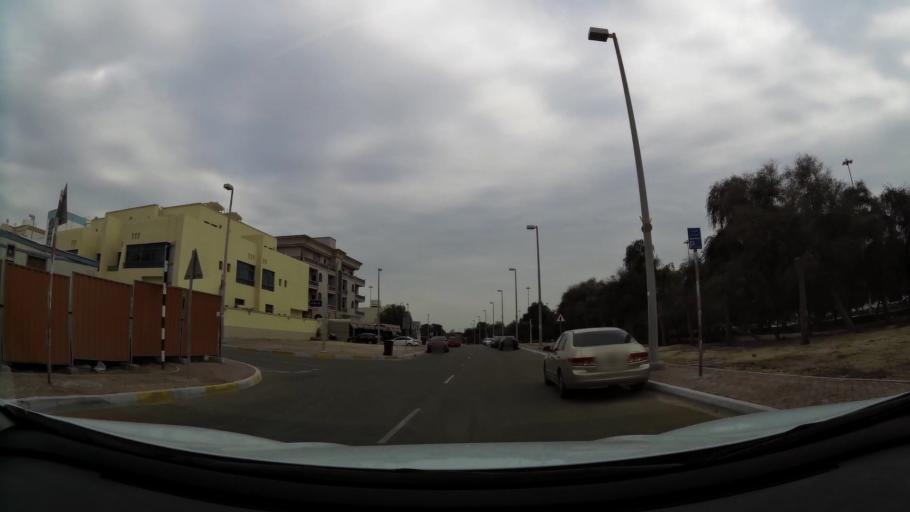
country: AE
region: Abu Dhabi
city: Abu Dhabi
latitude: 24.4379
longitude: 54.4029
